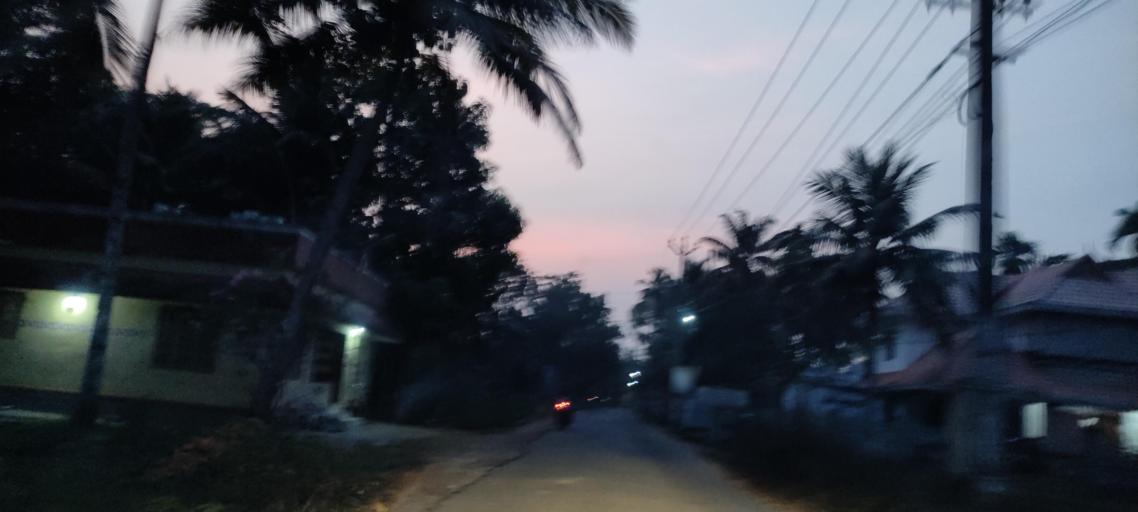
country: IN
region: Kerala
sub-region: Alappuzha
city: Mavelikara
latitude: 9.3213
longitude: 76.4499
